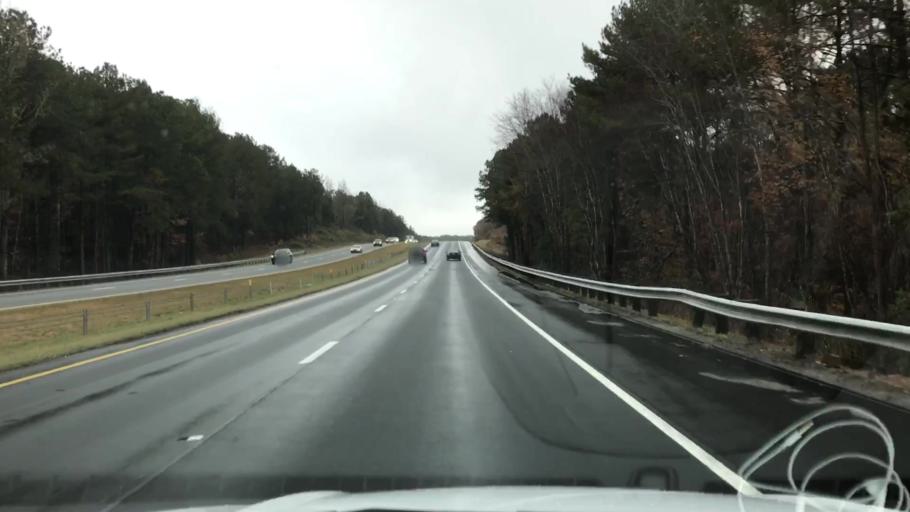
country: US
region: South Carolina
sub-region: Spartanburg County
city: Woodruff
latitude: 34.7239
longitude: -81.9478
